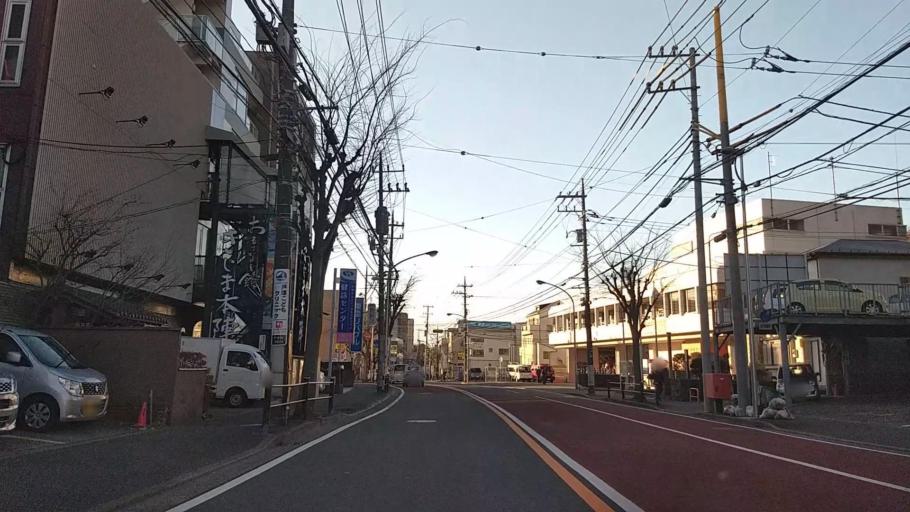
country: JP
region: Kanagawa
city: Fujisawa
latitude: 35.3985
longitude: 139.5309
